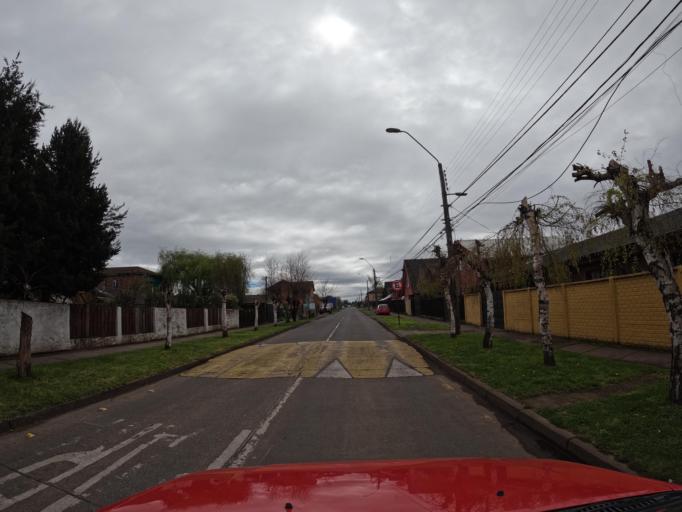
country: CL
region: Araucania
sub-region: Provincia de Malleco
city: Victoria
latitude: -38.2333
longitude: -72.3281
